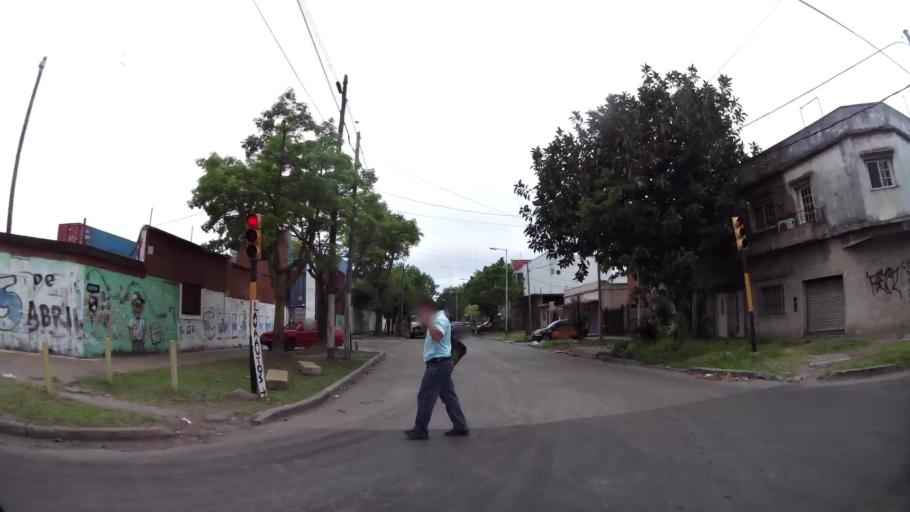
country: AR
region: Buenos Aires
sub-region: Partido de Avellaneda
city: Avellaneda
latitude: -34.6867
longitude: -58.3645
